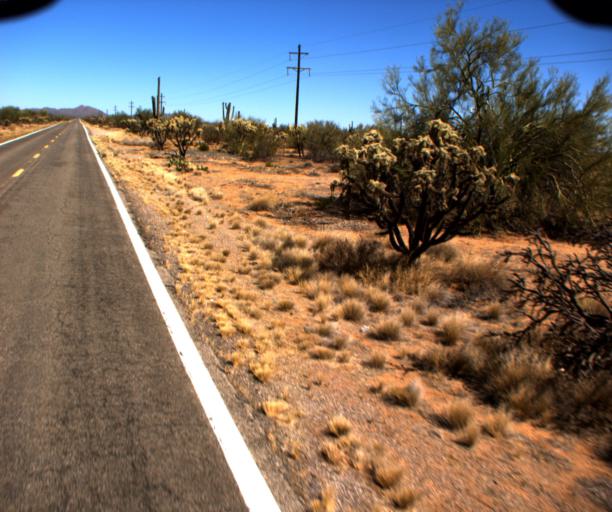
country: US
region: Arizona
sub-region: Pima County
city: Sells
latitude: 32.1077
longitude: -112.0716
